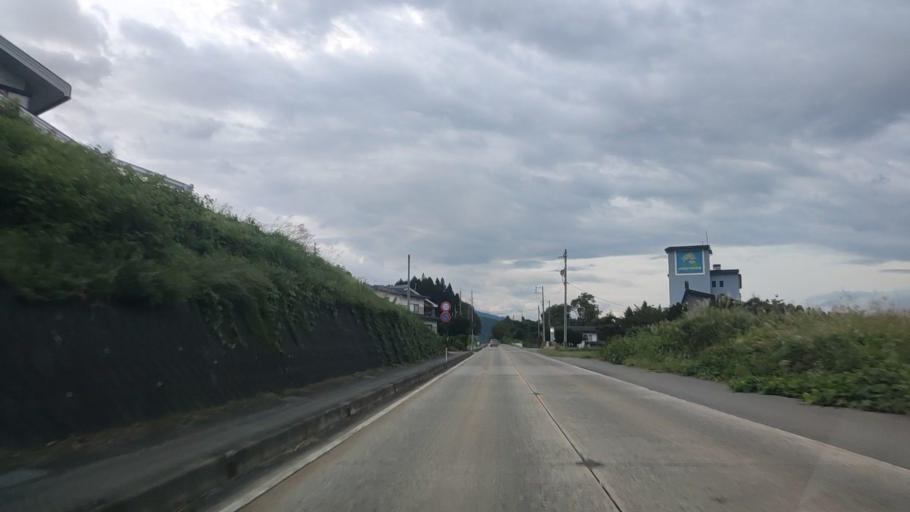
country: JP
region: Nagano
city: Iiyama
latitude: 36.8911
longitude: 138.4073
